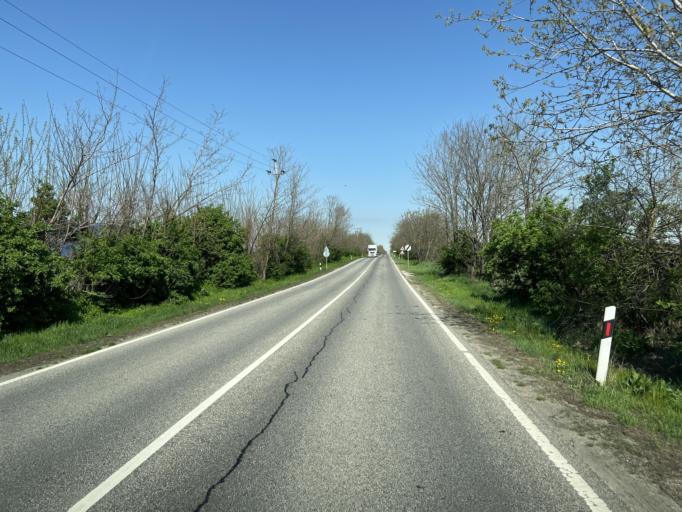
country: HU
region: Pest
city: Alsonemedi
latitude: 47.3336
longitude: 19.1815
